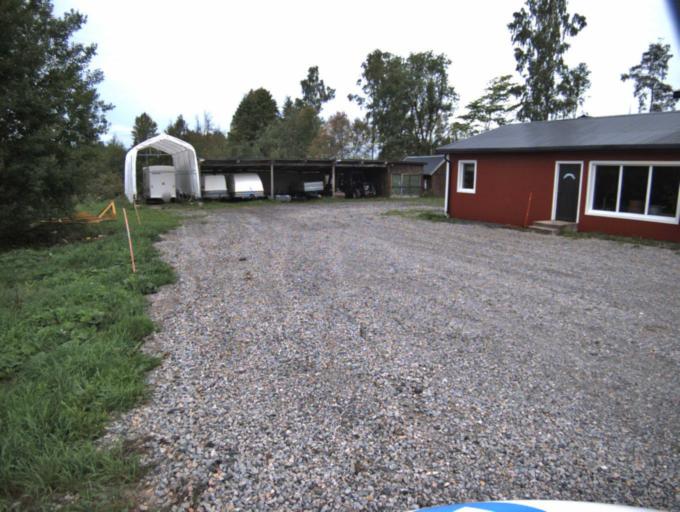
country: SE
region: Vaestra Goetaland
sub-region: Ulricehamns Kommun
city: Ulricehamn
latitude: 57.8048
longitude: 13.4434
